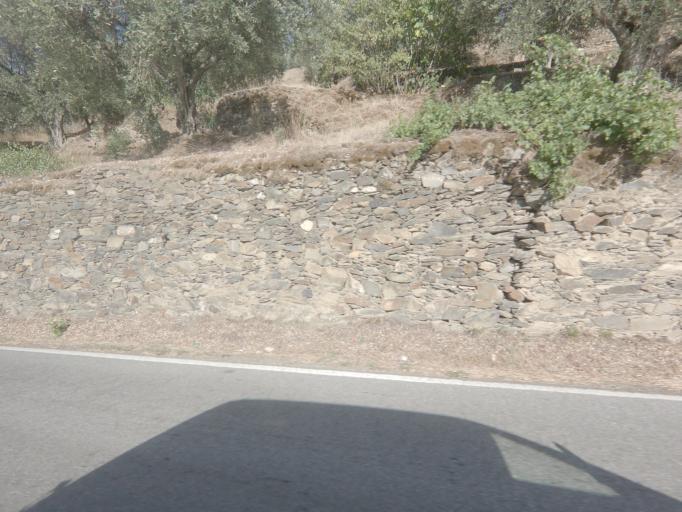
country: PT
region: Viseu
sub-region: Tabuaco
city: Tabuaco
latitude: 41.1755
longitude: -7.5530
